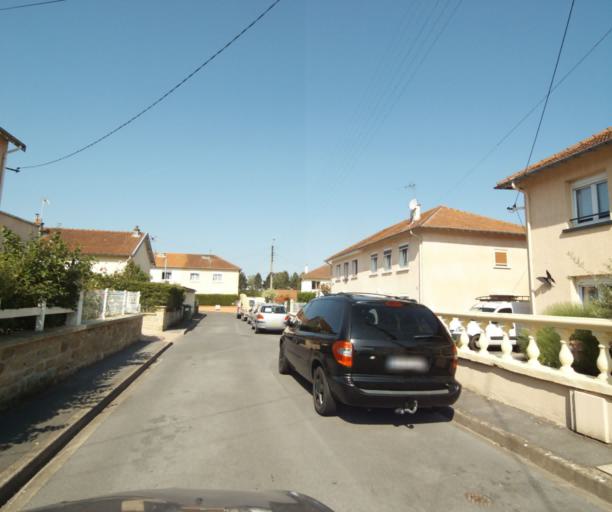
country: FR
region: Champagne-Ardenne
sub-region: Departement des Ardennes
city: Charleville-Mezieres
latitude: 49.7796
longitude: 4.7044
